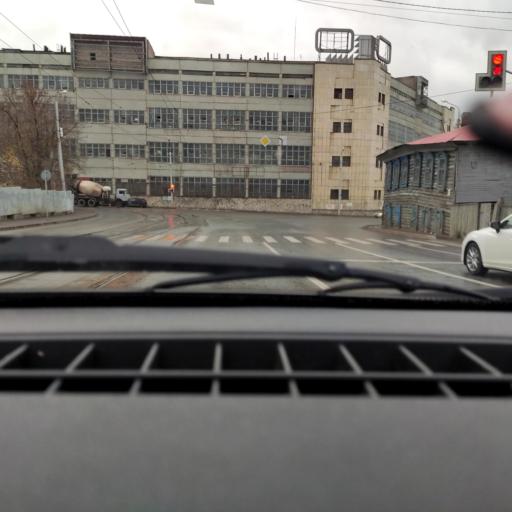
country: RU
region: Bashkortostan
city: Ufa
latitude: 54.7376
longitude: 55.9413
